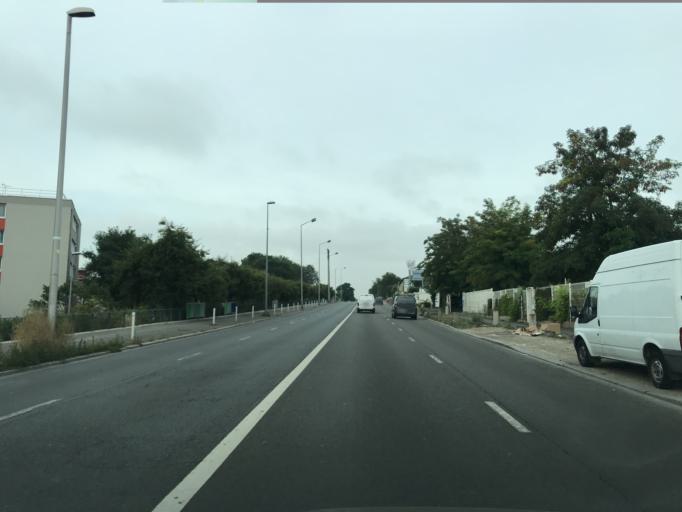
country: FR
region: Ile-de-France
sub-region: Departement de Seine-Saint-Denis
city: Drancy
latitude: 48.9115
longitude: 2.4337
